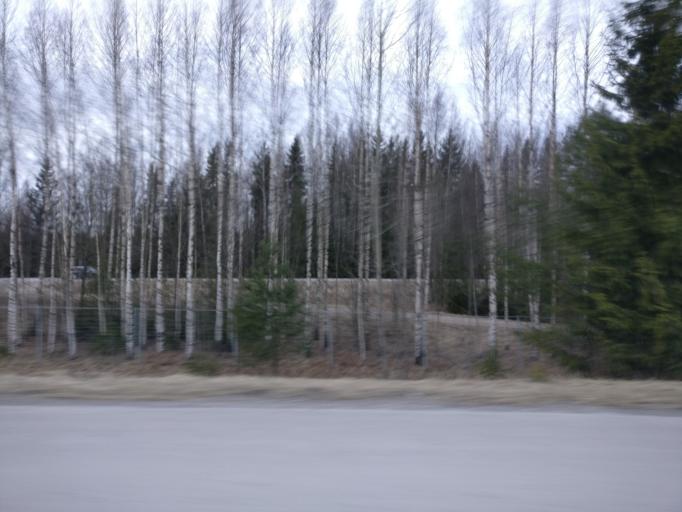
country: FI
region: Uusimaa
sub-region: Helsinki
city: Nurmijaervi
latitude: 60.4839
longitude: 24.8494
